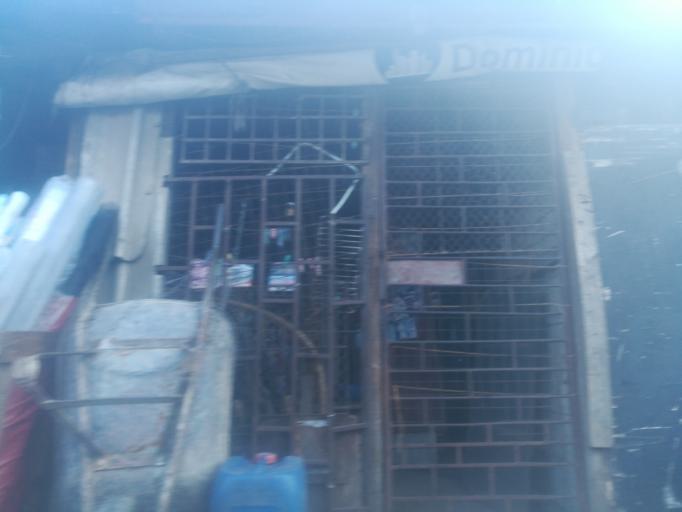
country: NG
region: Lagos
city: Somolu
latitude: 6.5406
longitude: 3.3857
